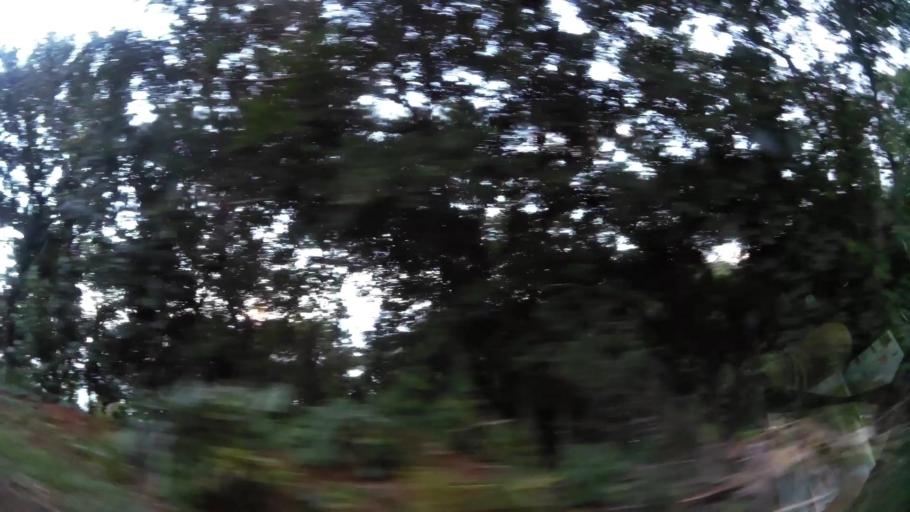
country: DM
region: Saint Andrew
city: Calibishie
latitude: 15.5923
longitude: -61.3560
